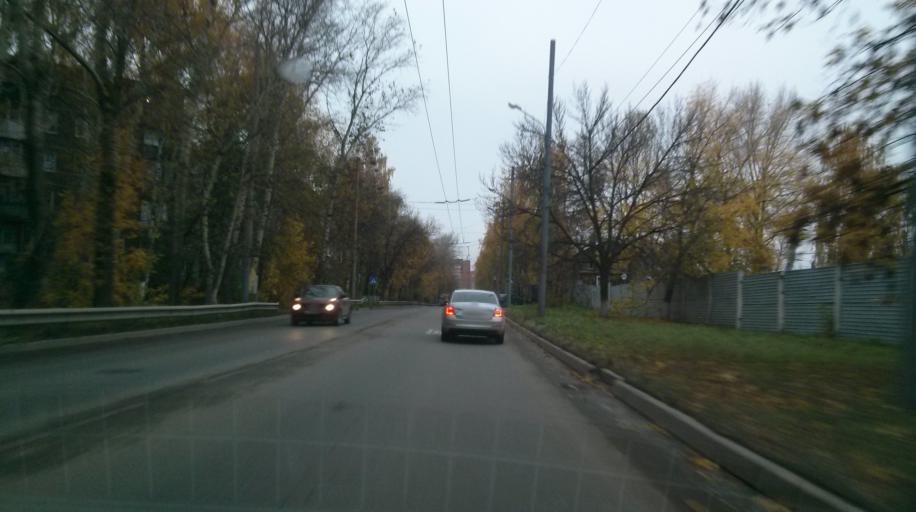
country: RU
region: Nizjnij Novgorod
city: Nizhniy Novgorod
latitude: 56.2985
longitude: 44.0500
